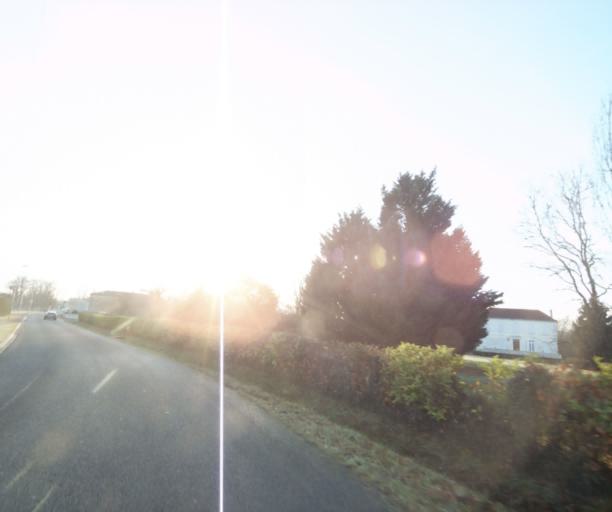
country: FR
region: Poitou-Charentes
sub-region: Departement de la Charente-Maritime
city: Fontcouverte
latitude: 45.7679
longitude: -0.5895
